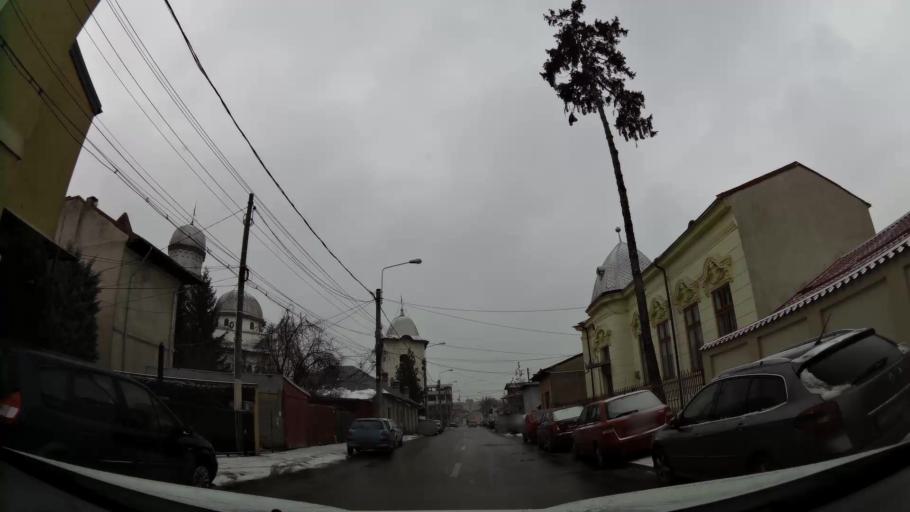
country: RO
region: Prahova
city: Ploiesti
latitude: 44.9498
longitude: 26.0195
